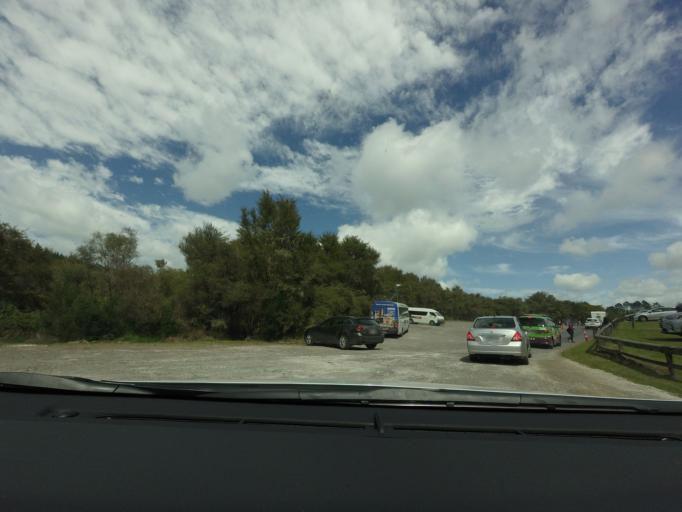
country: NZ
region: Bay of Plenty
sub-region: Rotorua District
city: Rotorua
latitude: -38.3501
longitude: 176.3775
